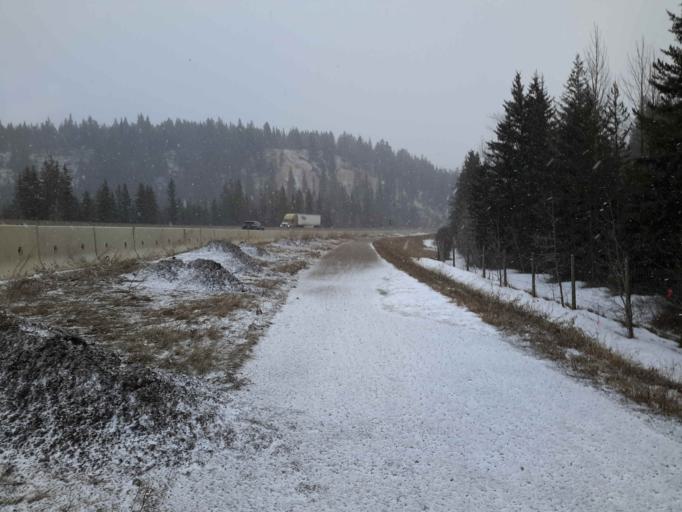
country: CA
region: Alberta
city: Banff
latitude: 51.2089
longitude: -115.5324
